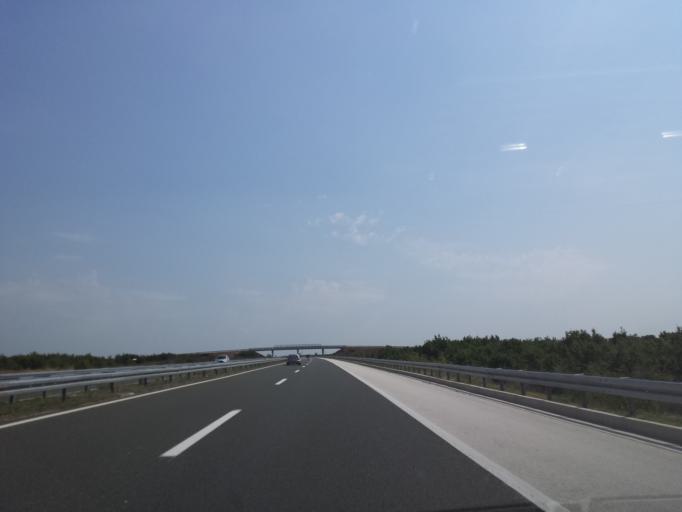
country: HR
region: Sibensko-Kniniska
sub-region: Grad Sibenik
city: Pirovac
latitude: 43.9292
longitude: 15.7182
